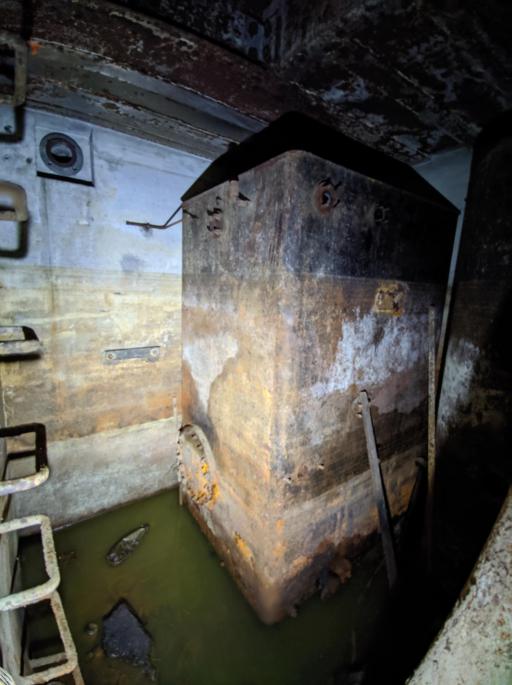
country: PL
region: Lubusz
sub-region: Powiat miedzyrzecki
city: Miedzyrzecz
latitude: 52.3810
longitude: 15.5048
